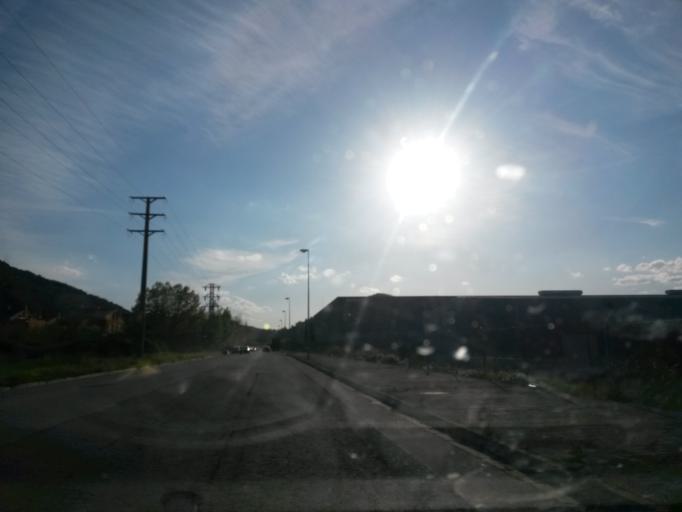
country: ES
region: Catalonia
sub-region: Provincia de Girona
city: Celra
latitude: 42.0296
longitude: 2.8732
